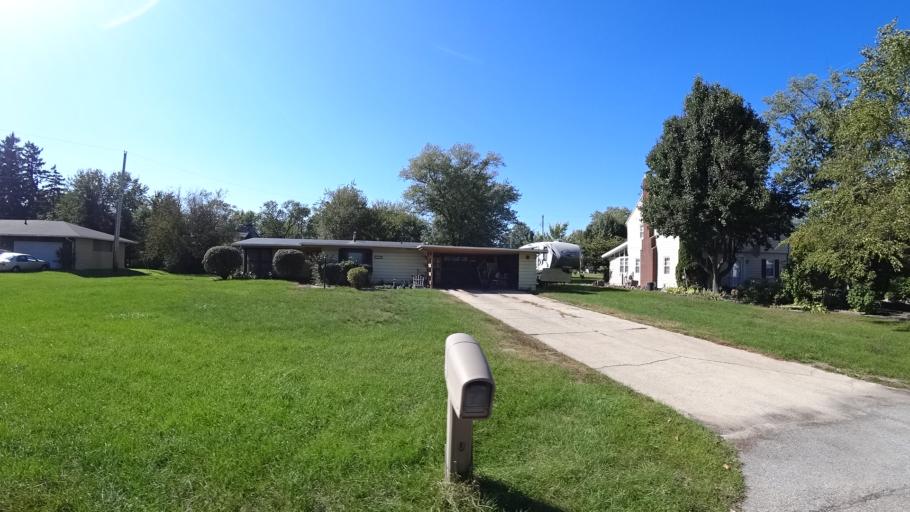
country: US
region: Indiana
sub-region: LaPorte County
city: Michigan City
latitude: 41.6924
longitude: -86.8911
